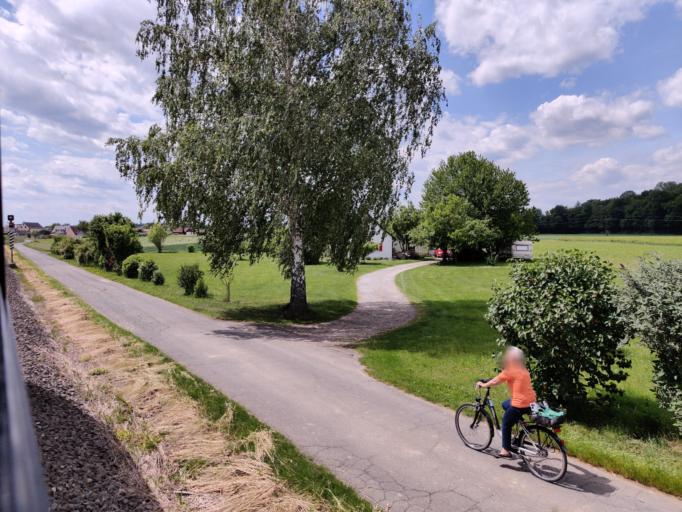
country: AT
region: Styria
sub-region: Politischer Bezirk Suedoststeiermark
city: Gosdorf
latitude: 46.7264
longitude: 15.8067
